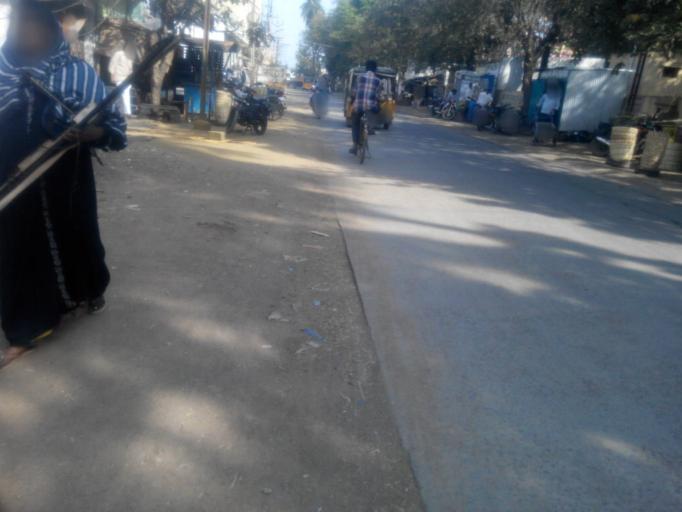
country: IN
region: Andhra Pradesh
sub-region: Kurnool
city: Nandyal
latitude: 15.4897
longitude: 78.4950
